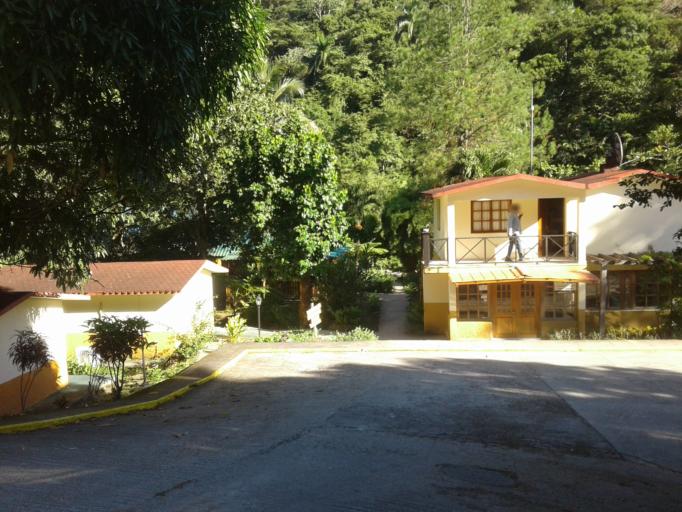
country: CU
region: Granma
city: Bartolome Maso
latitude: 20.0431
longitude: -76.9055
